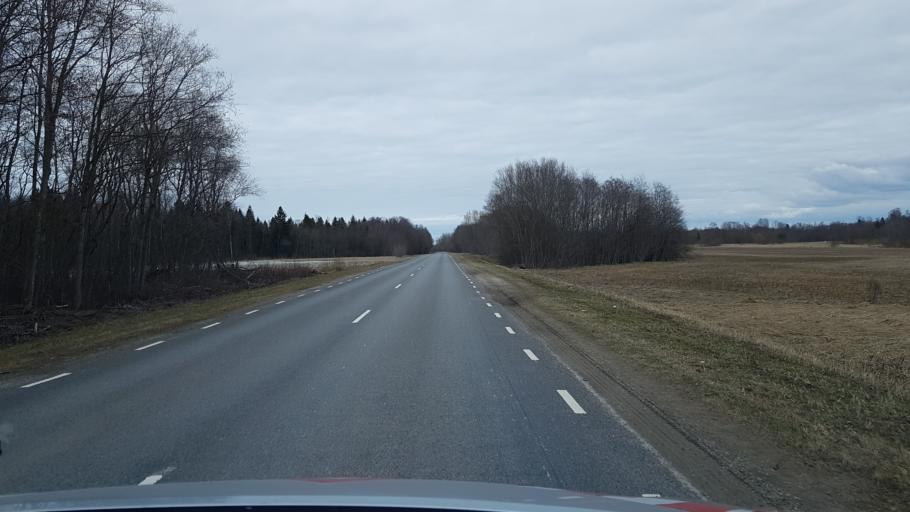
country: EE
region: Ida-Virumaa
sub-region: Sillamaee linn
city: Sillamae
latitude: 59.3572
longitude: 27.7502
